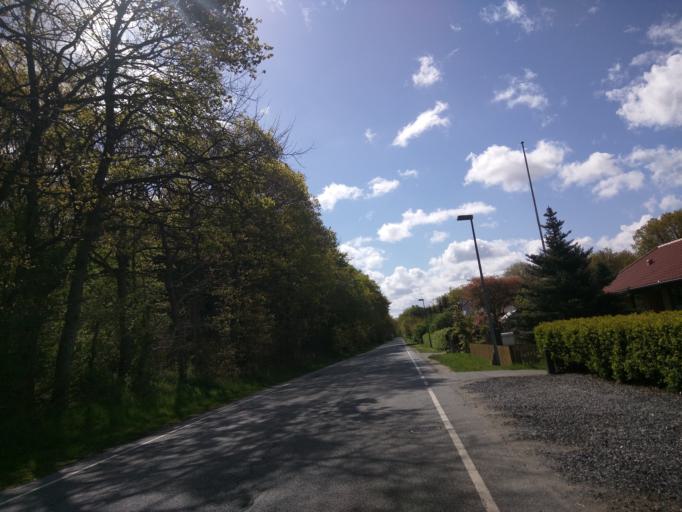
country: DK
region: Central Jutland
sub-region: Viborg Kommune
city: Viborg
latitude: 56.4114
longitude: 9.4185
